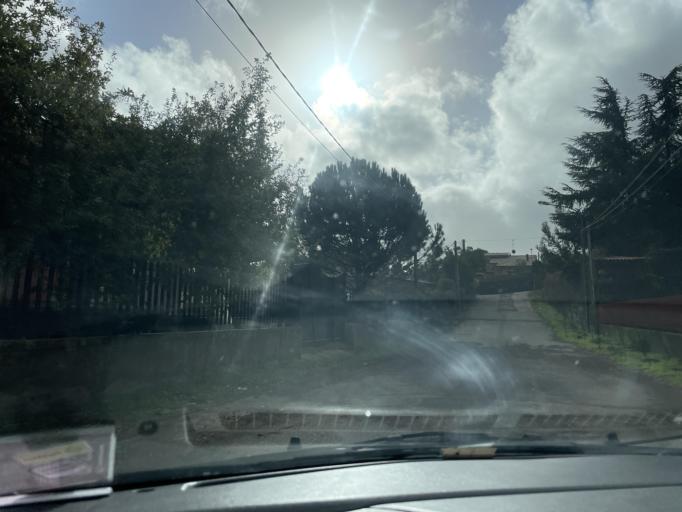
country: IT
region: Sicily
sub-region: Catania
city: Nicolosi
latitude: 37.6293
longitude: 15.0209
